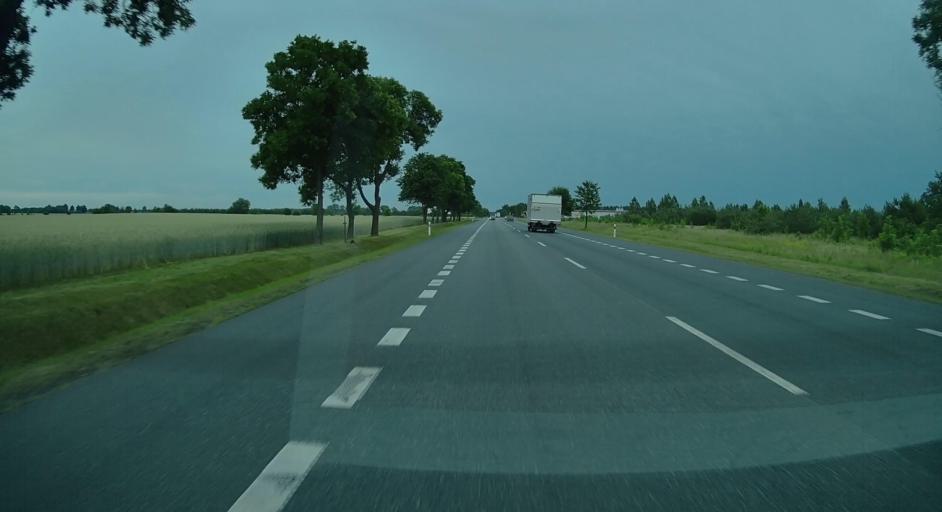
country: PL
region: Lublin Voivodeship
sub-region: Powiat bialski
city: Rokitno
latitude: 52.0359
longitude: 23.2438
